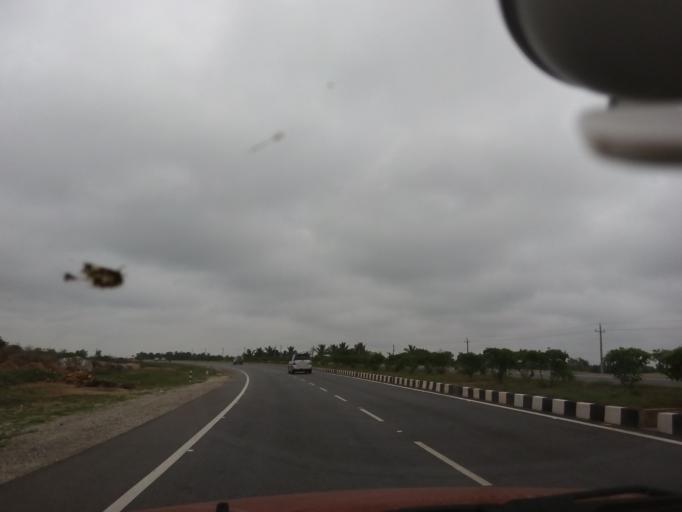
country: IN
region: Karnataka
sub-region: Hassan
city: Shravanabelagola
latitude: 12.9338
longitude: 76.5261
